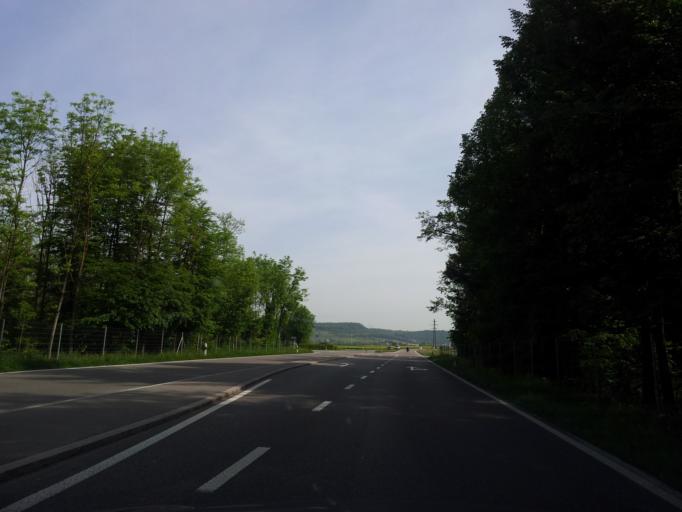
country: CH
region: Zurich
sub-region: Bezirk Buelach
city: Seglingen
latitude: 47.5899
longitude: 8.5284
